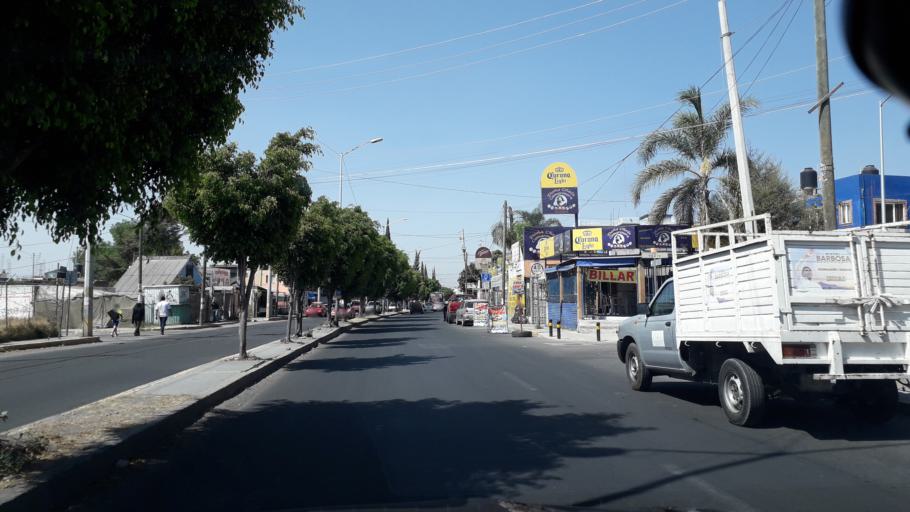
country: MX
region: Puebla
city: Puebla
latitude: 18.9892
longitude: -98.2148
